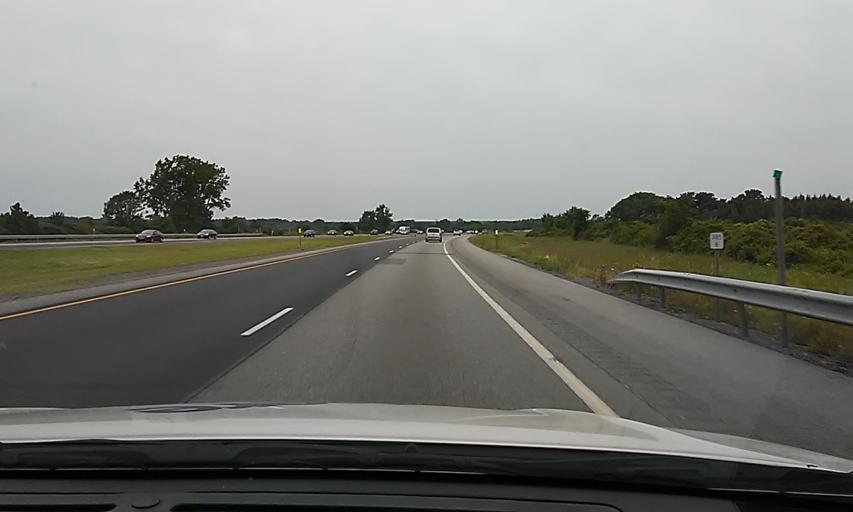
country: US
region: New York
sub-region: Genesee County
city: Batavia
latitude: 43.0138
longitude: -78.1033
